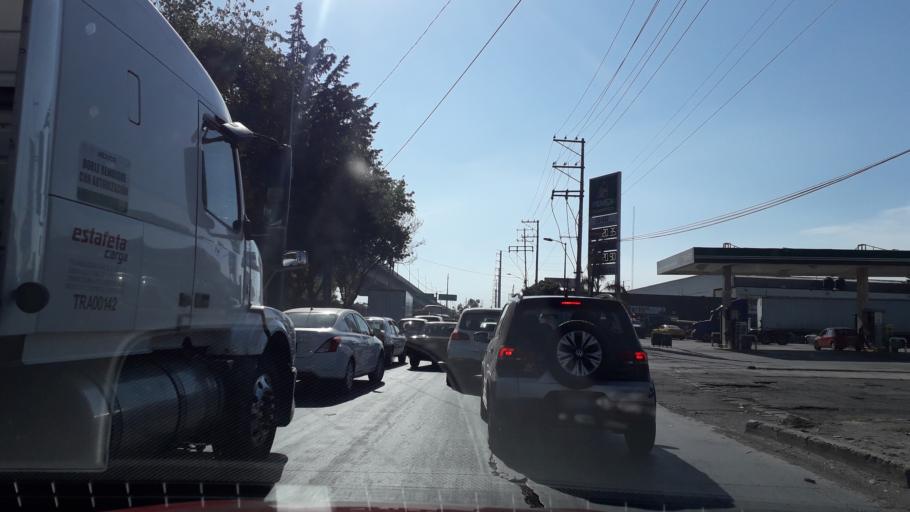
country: MX
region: Puebla
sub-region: Puebla
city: San Sebastian de Aparicio
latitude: 19.0846
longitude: -98.1894
